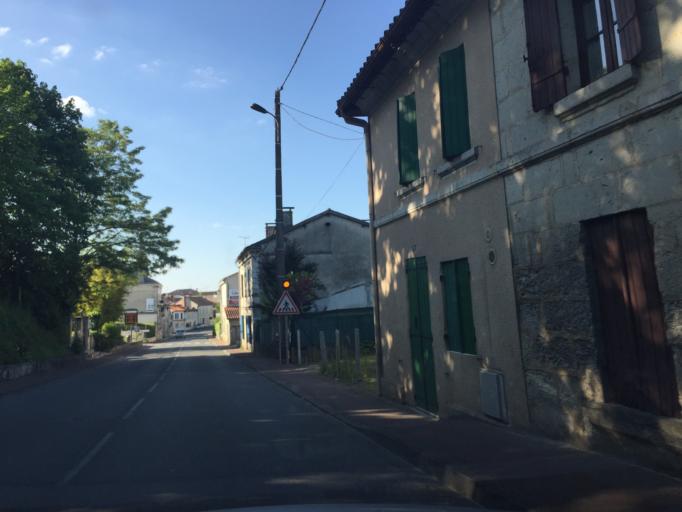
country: FR
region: Aquitaine
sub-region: Departement de la Dordogne
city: La Roche-Chalais
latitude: 45.1497
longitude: 0.0080
